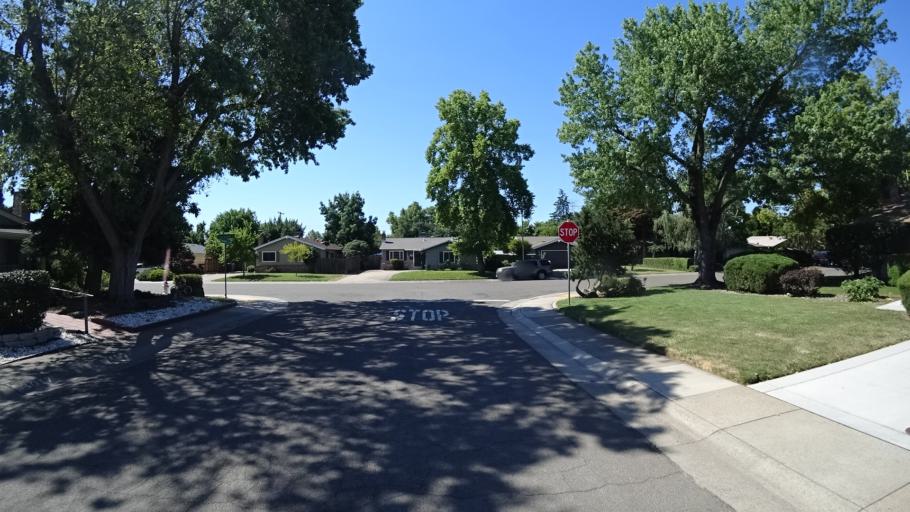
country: US
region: California
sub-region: Sacramento County
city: Rosemont
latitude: 38.5511
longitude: -121.3883
